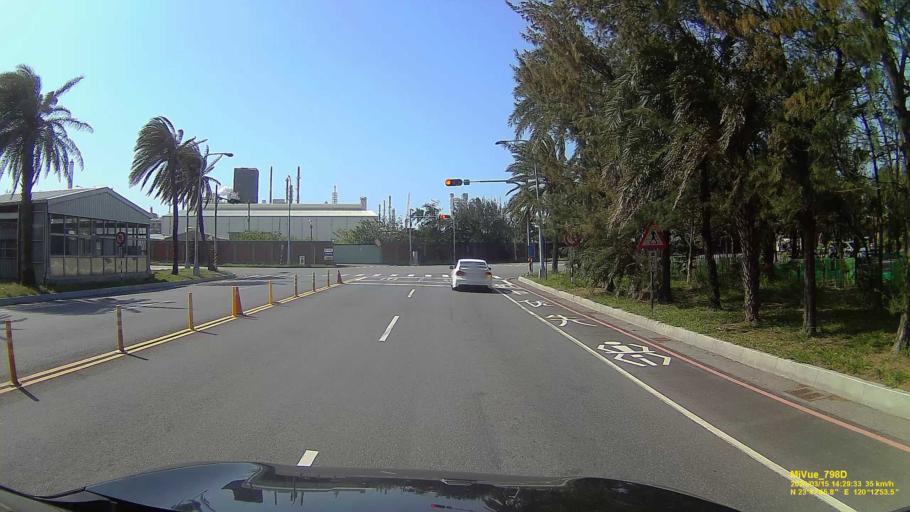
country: TW
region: Taiwan
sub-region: Yunlin
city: Douliu
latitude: 23.7962
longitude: 120.2148
